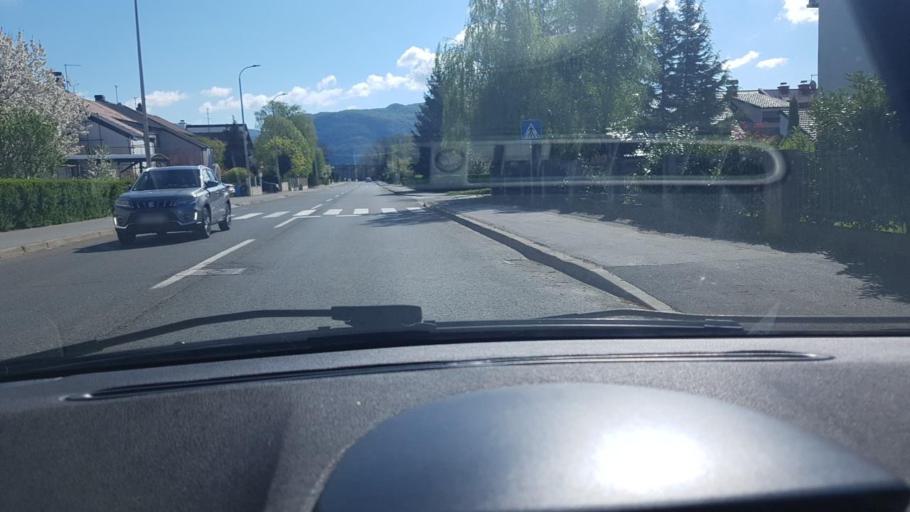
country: HR
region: Zagrebacka
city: Brdovec
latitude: 45.8696
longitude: 15.7977
